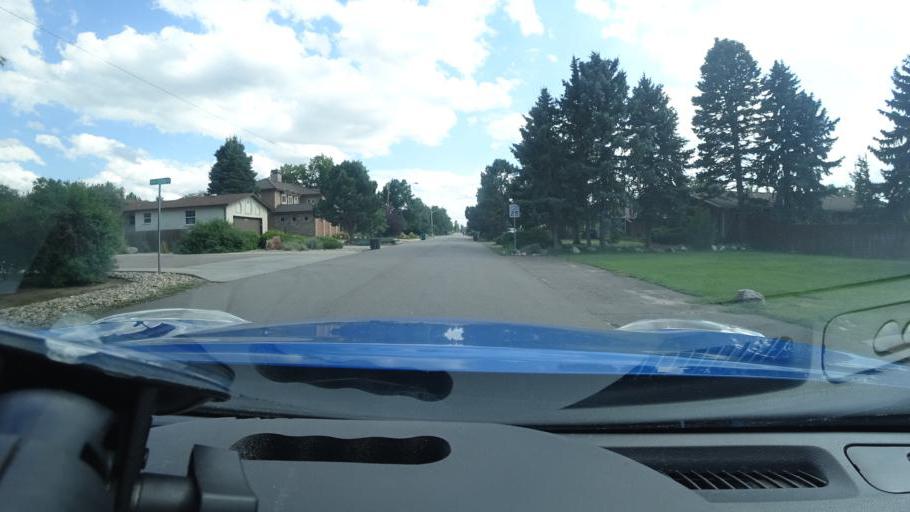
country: US
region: Colorado
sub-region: Adams County
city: Aurora
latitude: 39.7000
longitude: -104.8707
